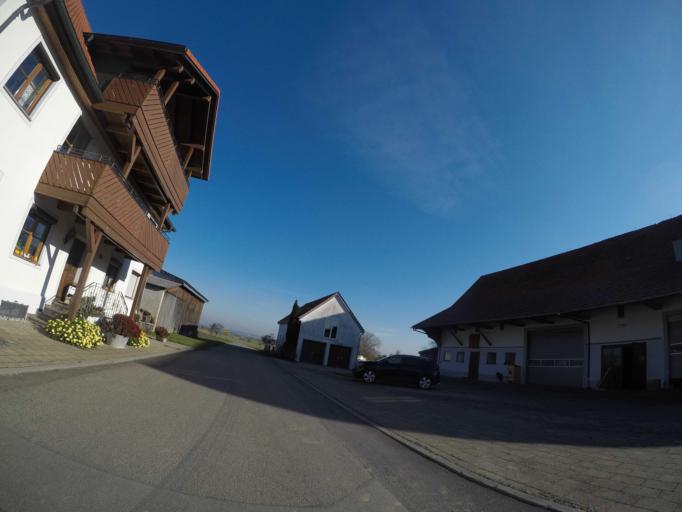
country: DE
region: Baden-Wuerttemberg
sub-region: Tuebingen Region
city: Hausen am Bussen
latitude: 48.2187
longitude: 9.6126
